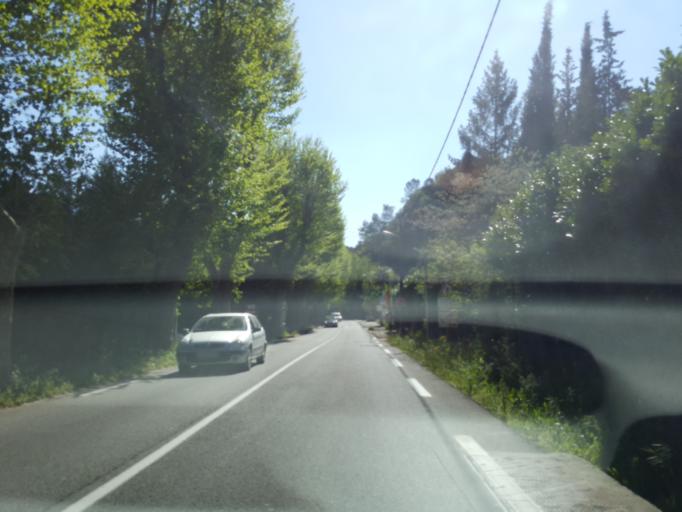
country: FR
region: Provence-Alpes-Cote d'Azur
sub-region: Departement du Var
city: Meounes-les-Montrieux
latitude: 43.2844
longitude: 5.9727
